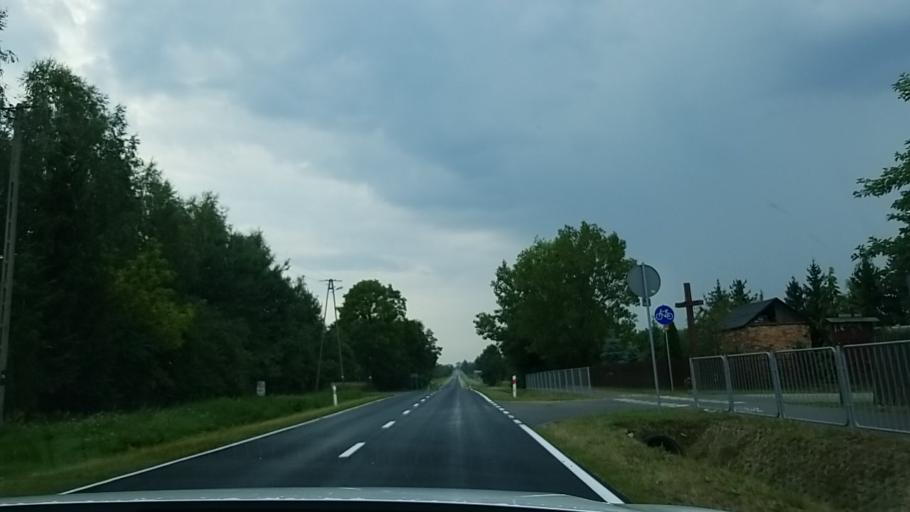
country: PL
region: Lublin Voivodeship
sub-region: Powiat wlodawski
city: Wlodawa
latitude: 51.5895
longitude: 23.5386
